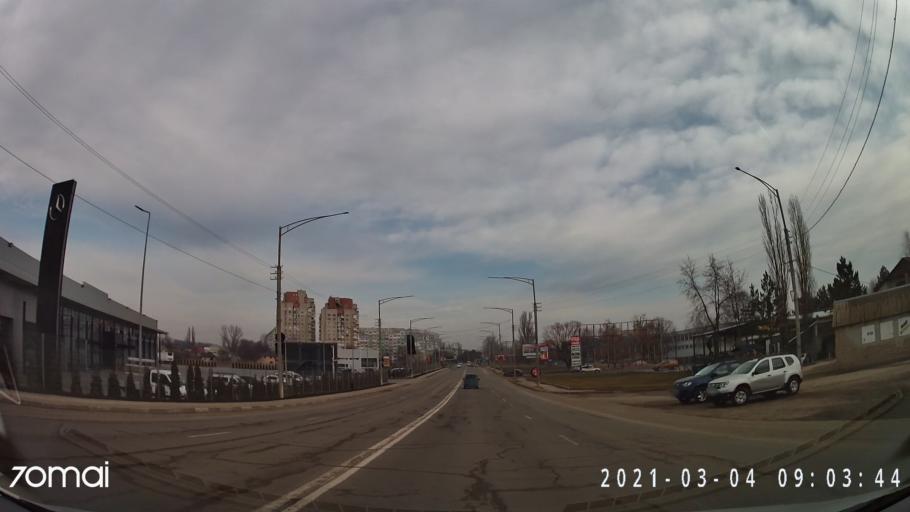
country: MD
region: Balti
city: Balti
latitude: 47.7527
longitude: 27.9430
